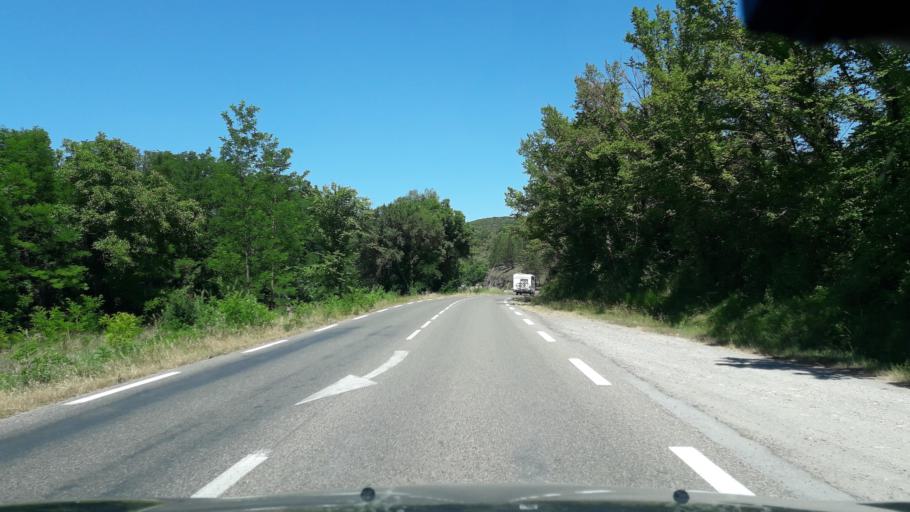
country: FR
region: Rhone-Alpes
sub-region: Departement de l'Ardeche
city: Ruoms
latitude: 44.4106
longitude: 4.2982
